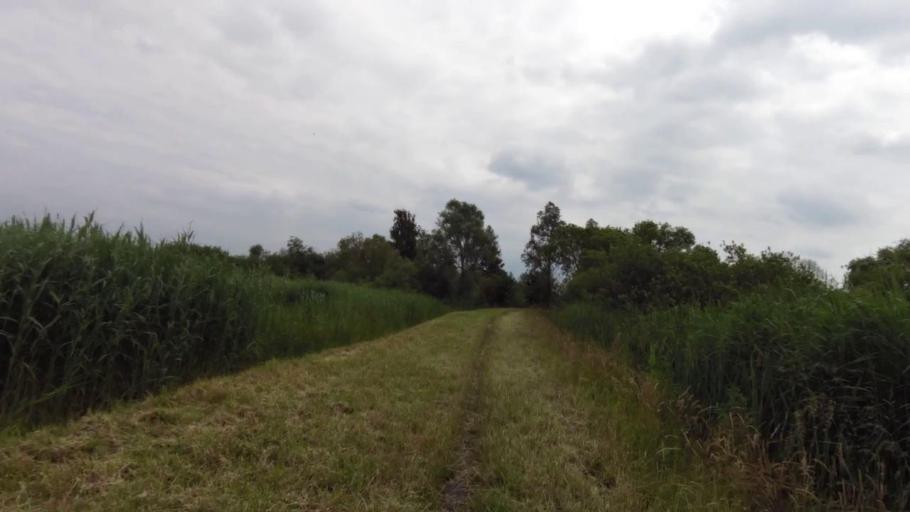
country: PL
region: West Pomeranian Voivodeship
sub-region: Szczecin
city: Szczecin
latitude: 53.4286
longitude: 14.6544
